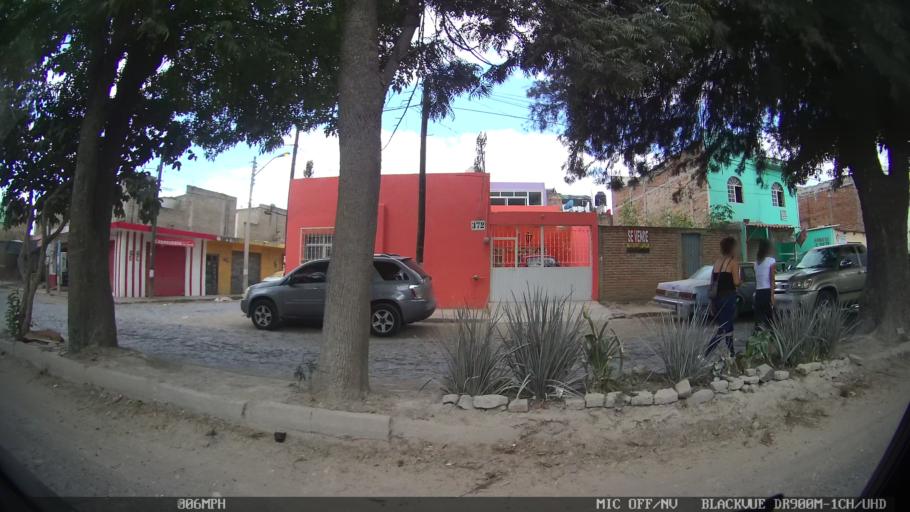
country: MX
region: Jalisco
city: Tonala
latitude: 20.6632
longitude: -103.2520
